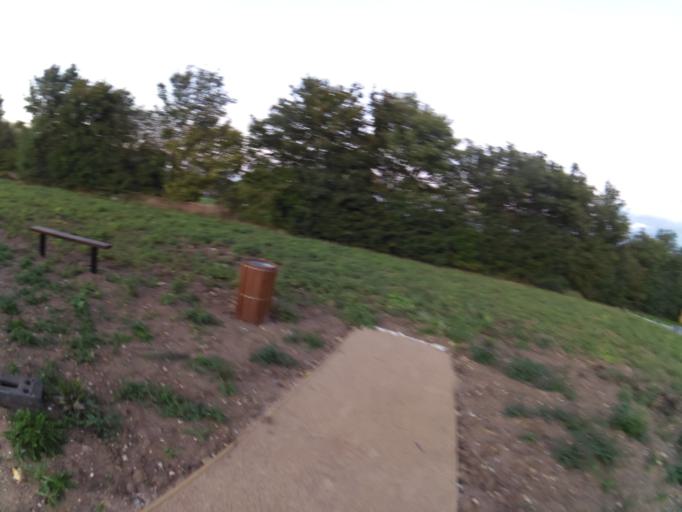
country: GB
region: England
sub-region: Suffolk
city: Bramford
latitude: 52.0816
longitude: 1.0955
